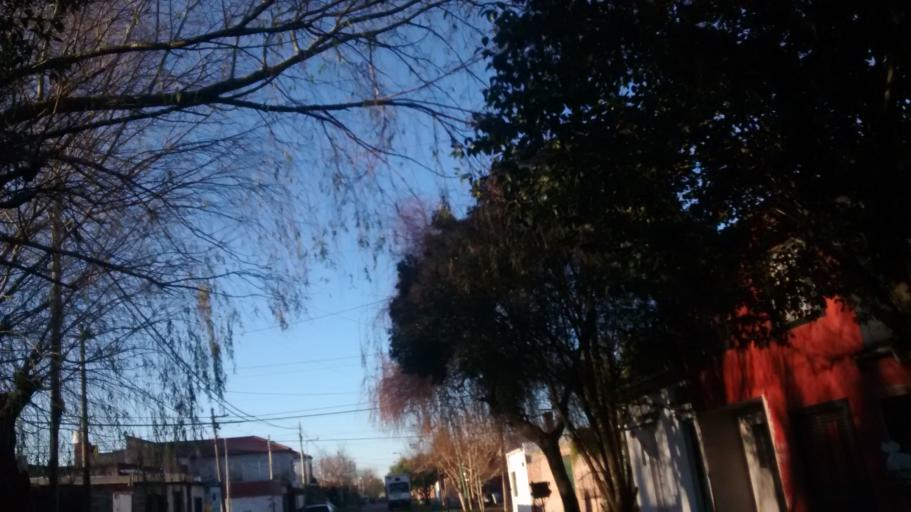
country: AR
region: Buenos Aires
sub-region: Partido de La Plata
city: La Plata
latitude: -34.9571
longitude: -57.9396
